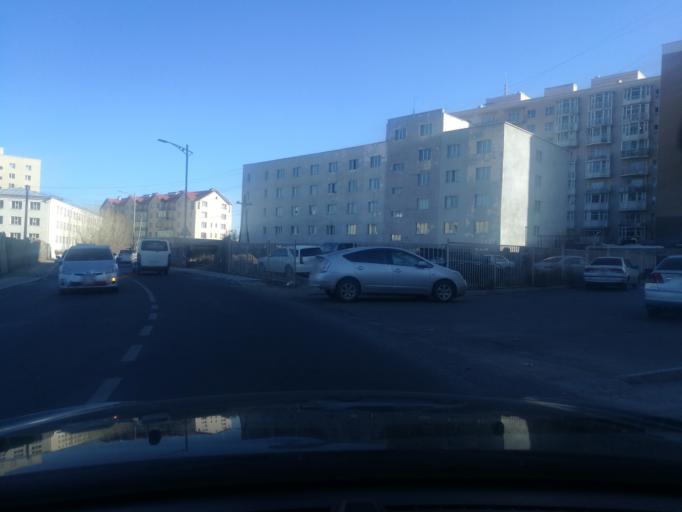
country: MN
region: Ulaanbaatar
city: Ulaanbaatar
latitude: 47.8863
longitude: 106.9048
